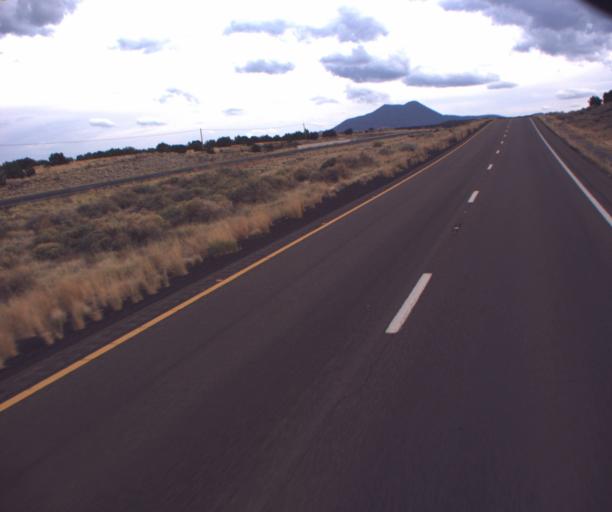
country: US
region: Arizona
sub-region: Coconino County
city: Flagstaff
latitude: 35.5194
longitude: -111.5440
